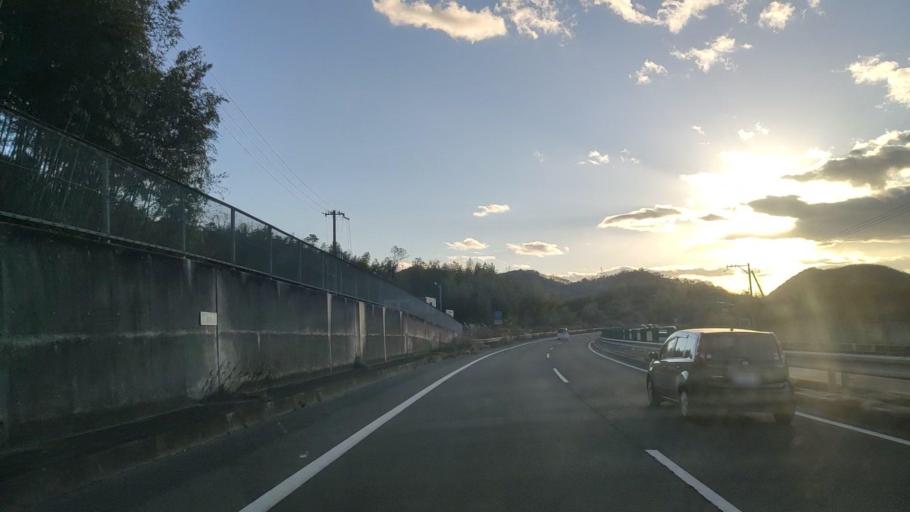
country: JP
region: Hyogo
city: Tatsunocho-tominaga
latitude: 34.8615
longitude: 134.6176
